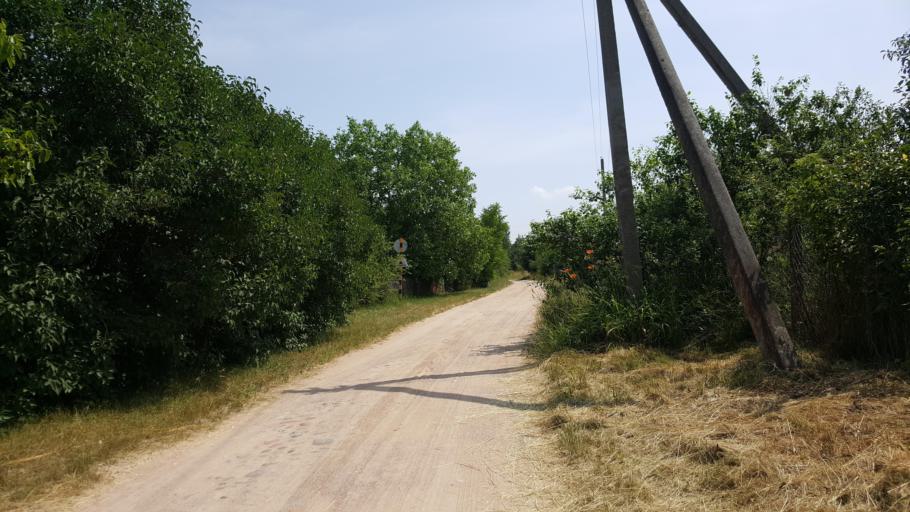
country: BY
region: Brest
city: Kamyanyets
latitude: 52.3540
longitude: 23.7542
